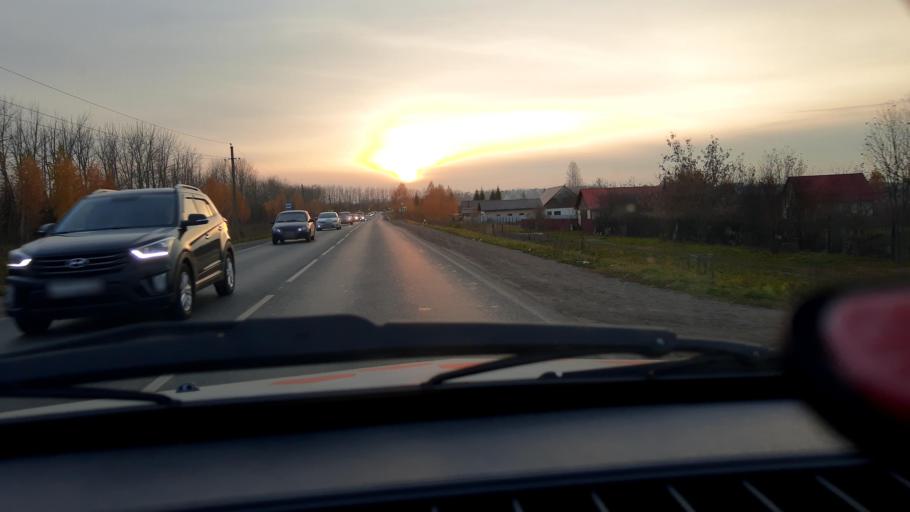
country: RU
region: Bashkortostan
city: Iglino
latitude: 54.7938
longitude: 56.2926
